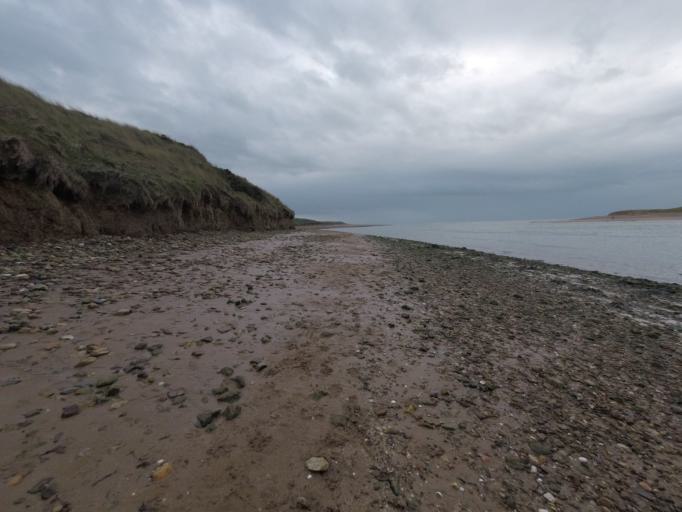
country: IE
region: Munster
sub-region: Waterford
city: Tra Mhor
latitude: 52.1507
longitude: -7.0864
